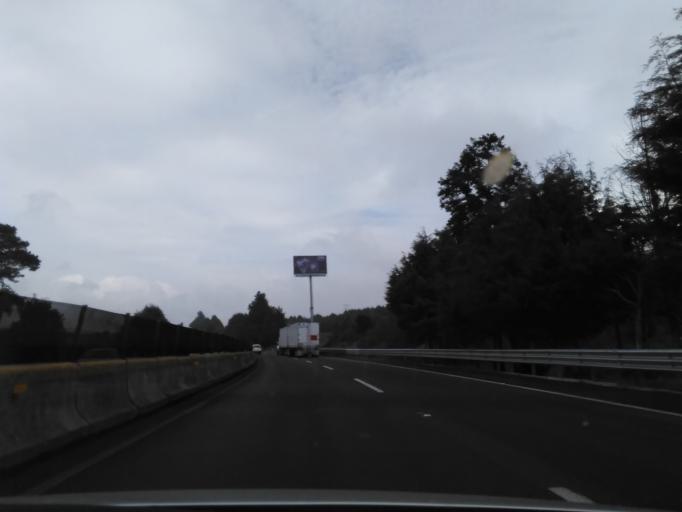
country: MX
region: Morelos
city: Tres Marias
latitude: 19.1132
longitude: -99.1834
